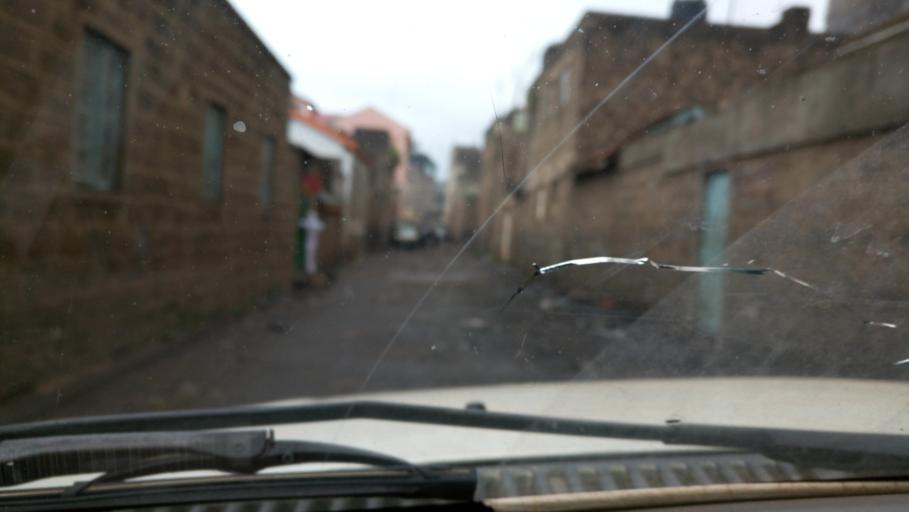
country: KE
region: Nairobi Area
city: Nairobi
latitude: -1.2783
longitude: 36.8283
